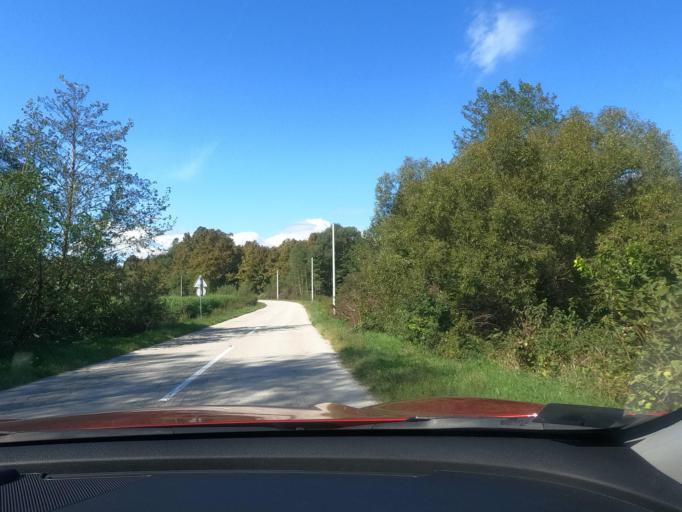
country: BA
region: Federation of Bosnia and Herzegovina
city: Vrnograc
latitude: 45.2418
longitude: 15.9432
